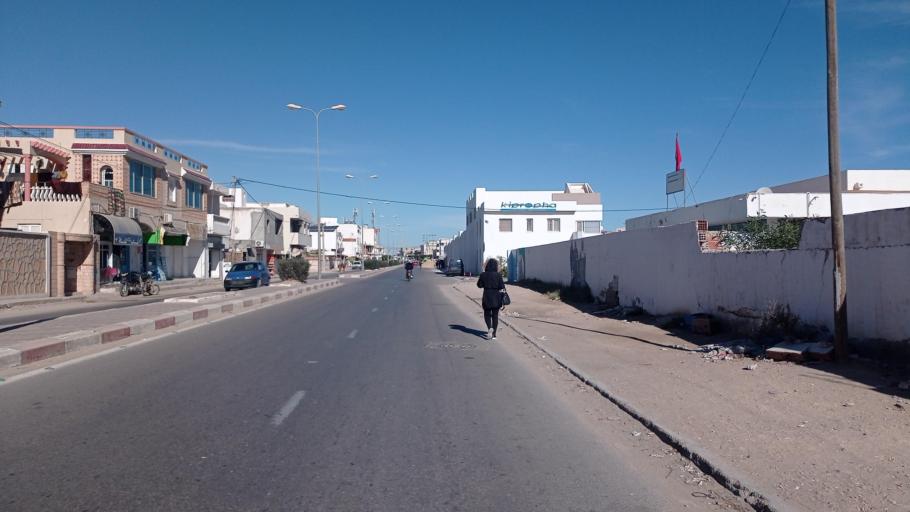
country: TN
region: Qabis
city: Gabes
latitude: 33.8422
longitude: 10.1139
